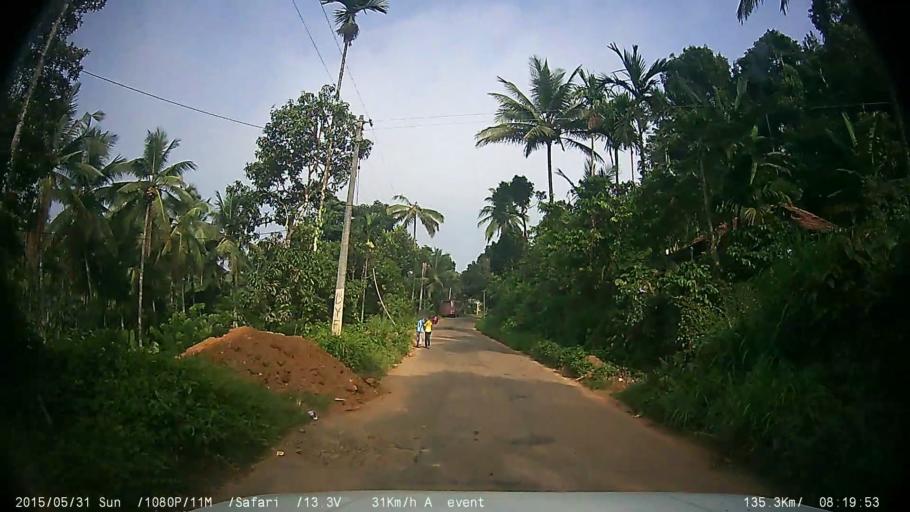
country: IN
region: Kerala
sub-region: Wayanad
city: Kalpetta
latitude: 11.6704
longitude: 75.9816
